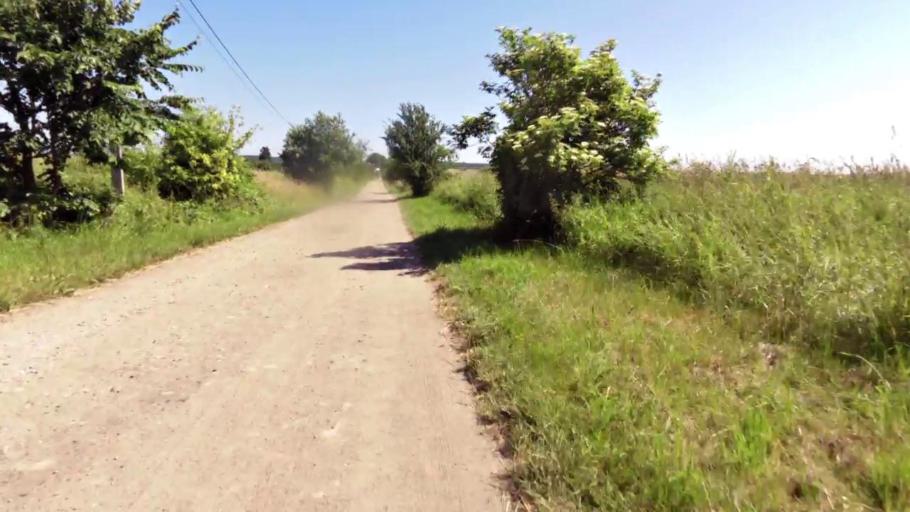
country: PL
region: West Pomeranian Voivodeship
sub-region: Powiat swidwinski
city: Rabino
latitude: 53.8465
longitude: 16.0009
